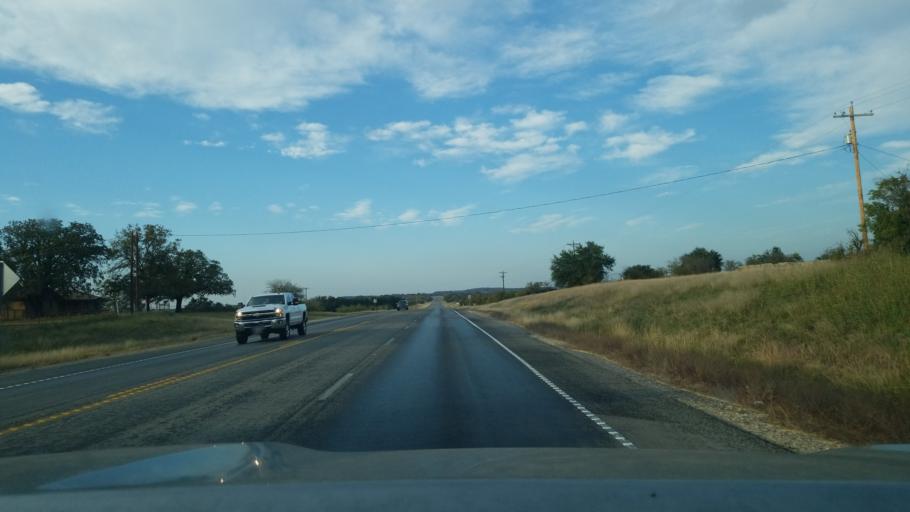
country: US
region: Texas
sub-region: Brown County
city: Lake Brownwood
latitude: 31.9903
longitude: -98.9208
